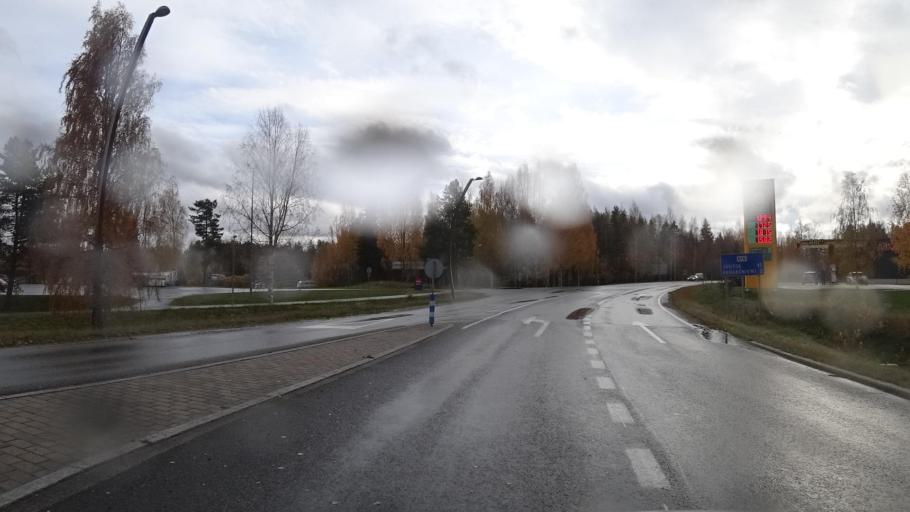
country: FI
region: Southern Savonia
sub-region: Mikkeli
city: Kangasniemi
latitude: 62.0029
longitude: 26.6567
